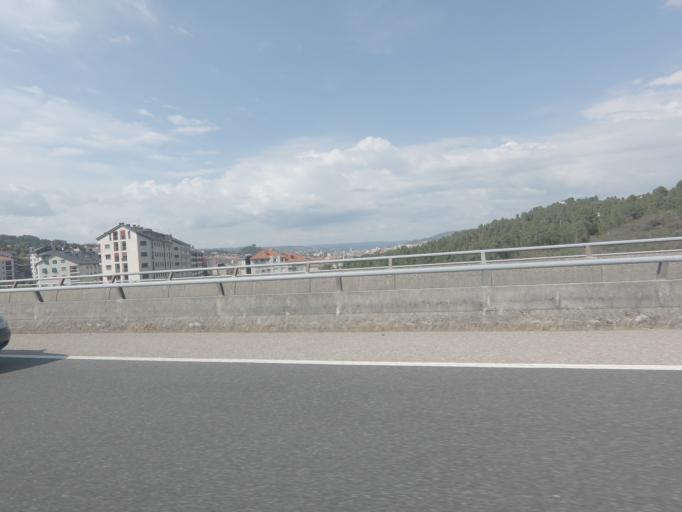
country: ES
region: Galicia
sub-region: Provincia de Ourense
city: Ourense
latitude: 42.3116
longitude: -7.8833
